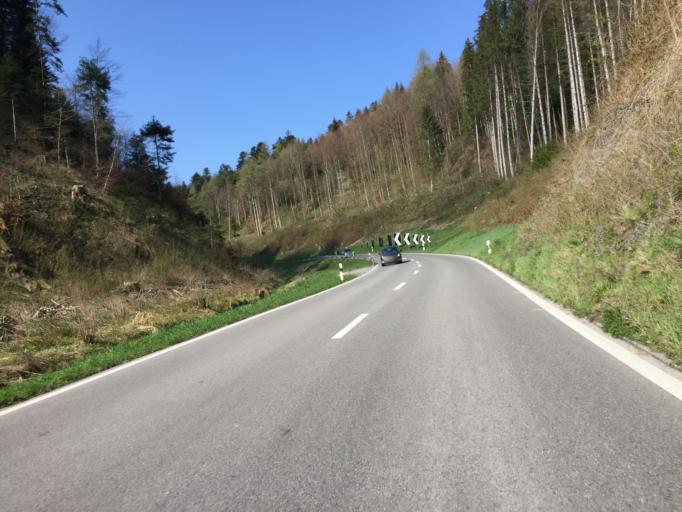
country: CH
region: Bern
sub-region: Bern-Mittelland District
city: Bariswil
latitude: 46.9981
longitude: 7.5250
